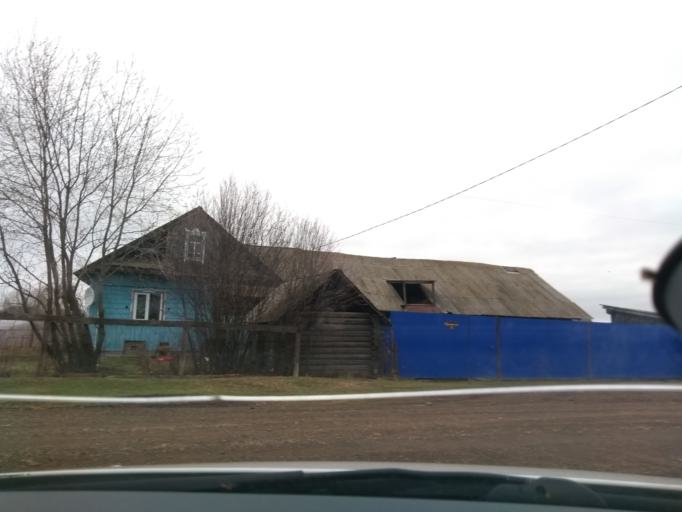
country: RU
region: Perm
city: Orda
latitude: 57.2173
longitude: 56.6009
